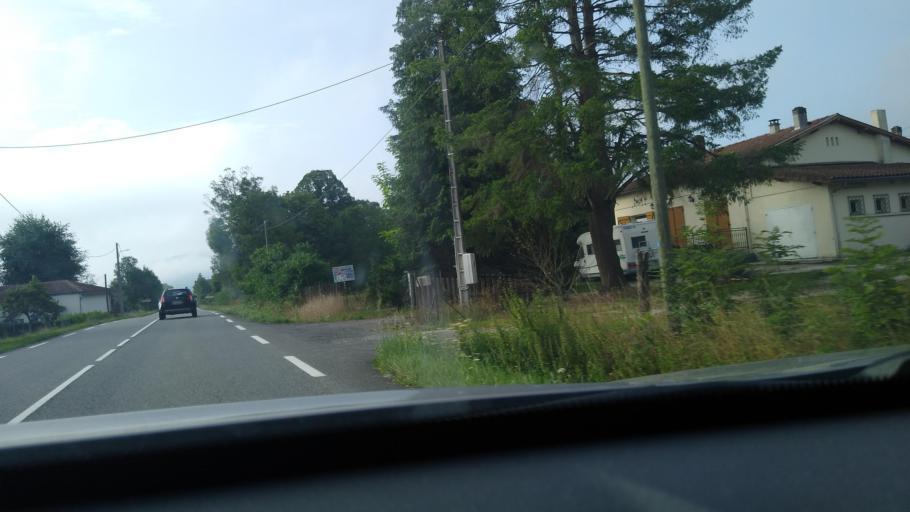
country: FR
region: Midi-Pyrenees
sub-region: Departement de la Haute-Garonne
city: Salies-du-Salat
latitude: 43.0602
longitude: 0.9744
